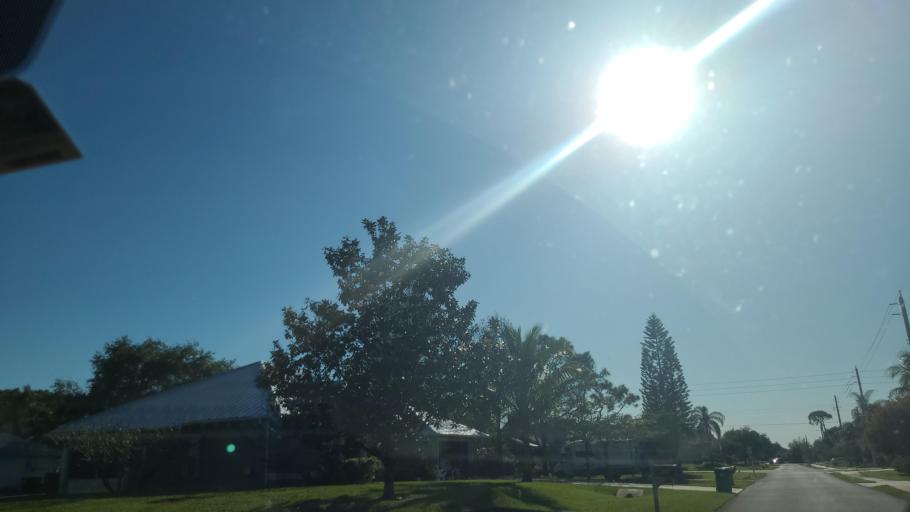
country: US
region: Florida
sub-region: Indian River County
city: Sebastian
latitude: 27.8072
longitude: -80.4854
